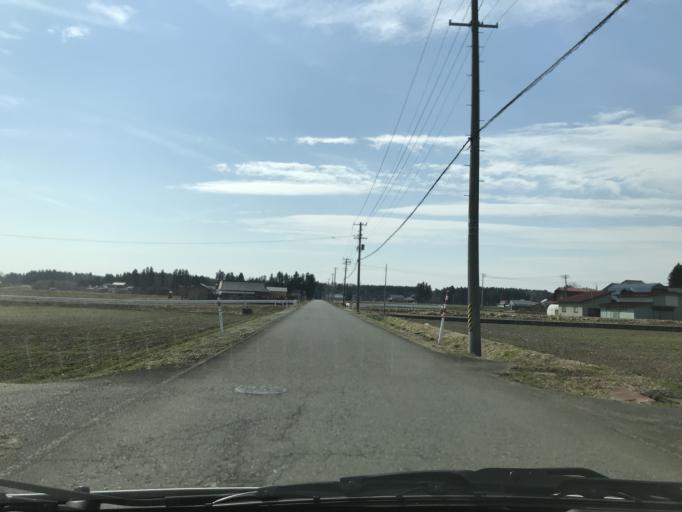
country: JP
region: Iwate
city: Mizusawa
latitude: 39.1267
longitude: 141.0435
